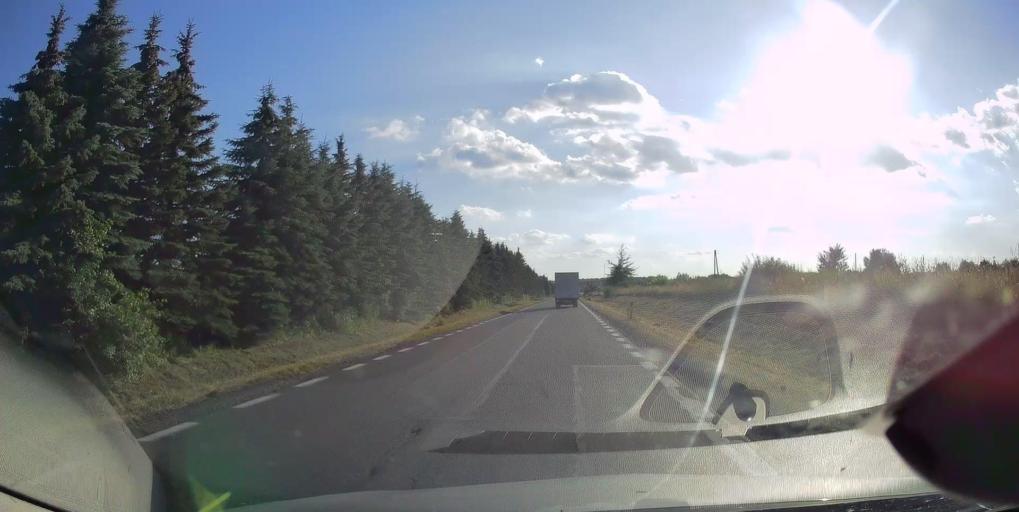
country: PL
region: Lodz Voivodeship
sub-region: Powiat rawski
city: Biala Rawska
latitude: 51.8032
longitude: 20.4594
